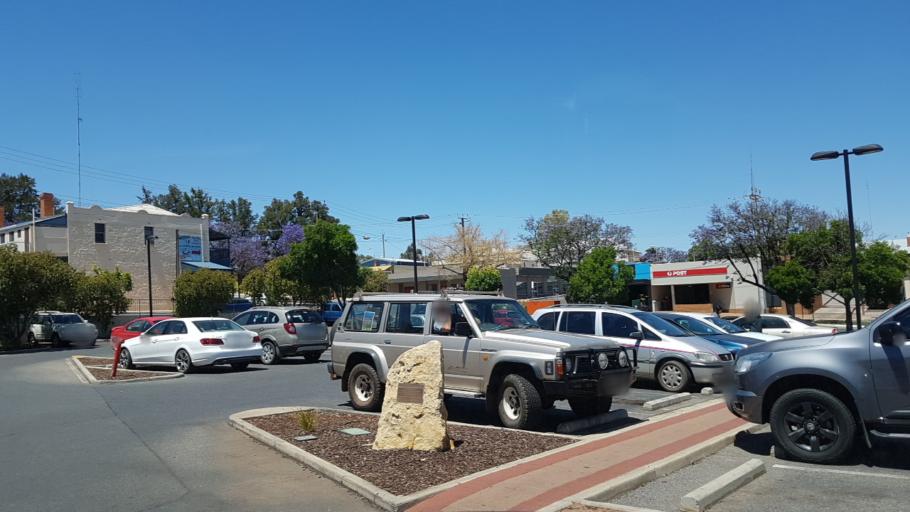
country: AU
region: South Australia
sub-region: Loxton Waikerie
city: Waikerie
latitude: -34.1786
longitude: 139.9862
